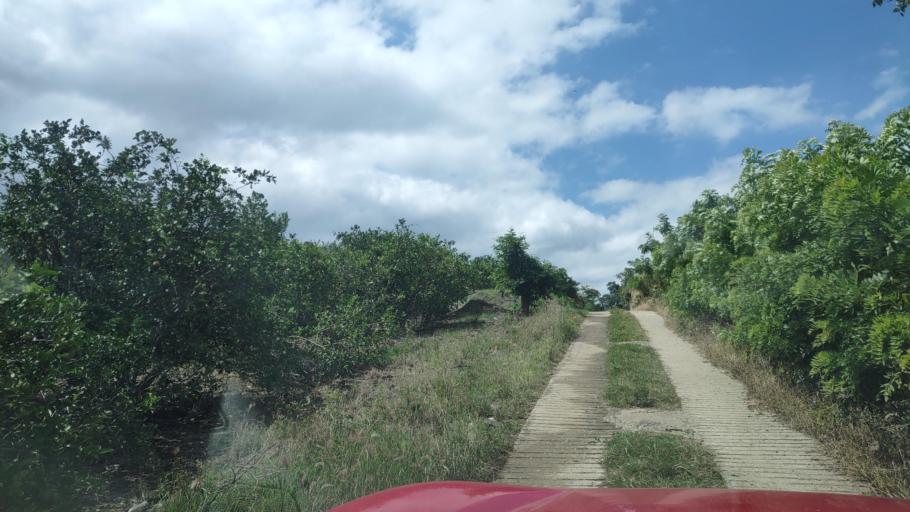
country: MX
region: Puebla
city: San Jose Acateno
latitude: 20.2195
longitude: -97.1411
